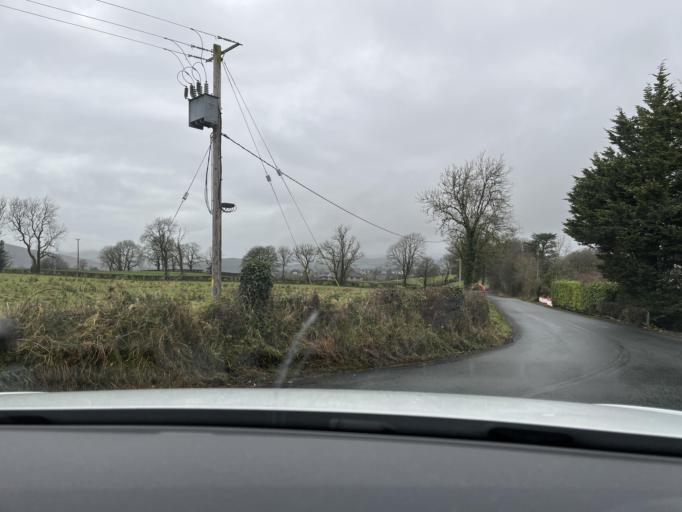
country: IE
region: Connaught
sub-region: County Leitrim
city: Manorhamilton
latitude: 54.3002
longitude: -8.1517
